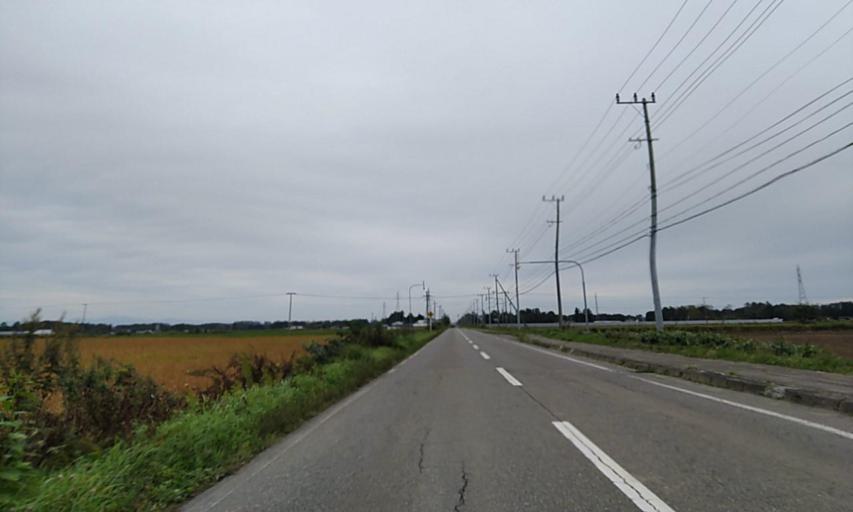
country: JP
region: Hokkaido
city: Obihiro
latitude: 42.6792
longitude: 143.1196
